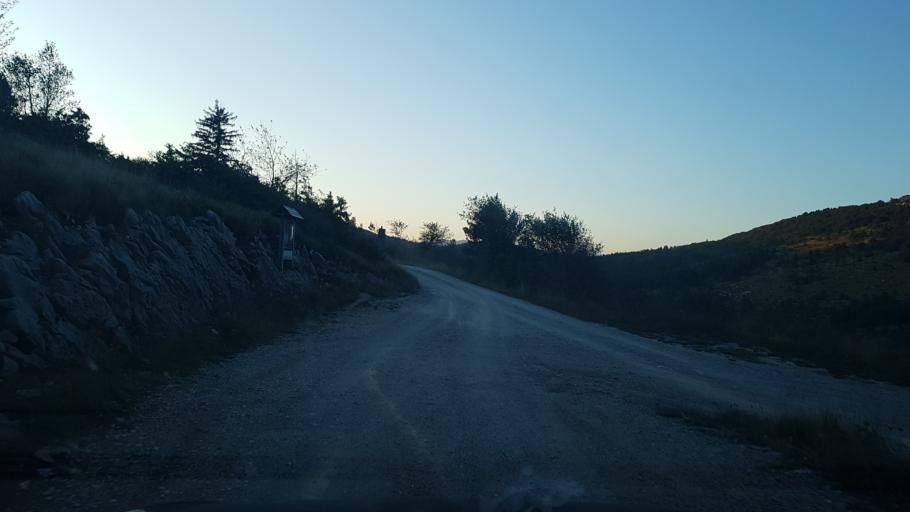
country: SI
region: Vipava
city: Vipava
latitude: 45.7922
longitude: 14.0213
